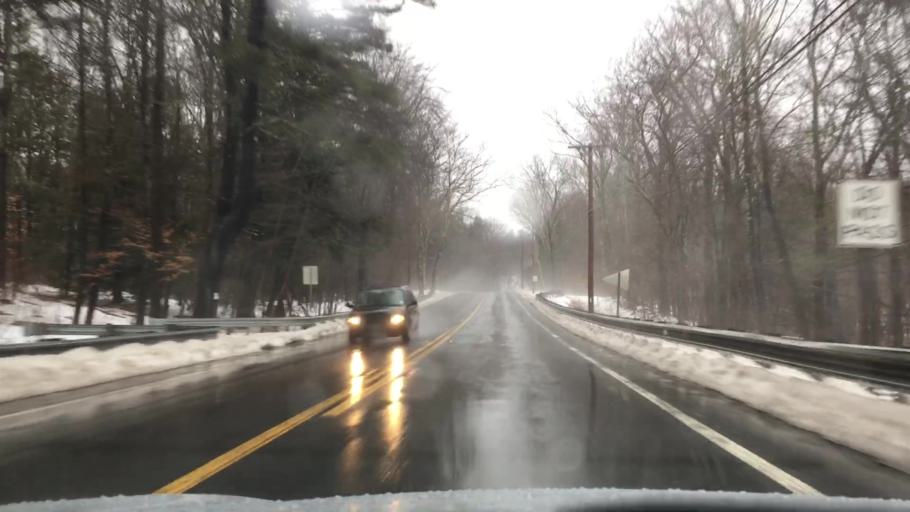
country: US
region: Massachusetts
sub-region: Hampshire County
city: Belchertown
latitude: 42.3182
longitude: -72.4064
